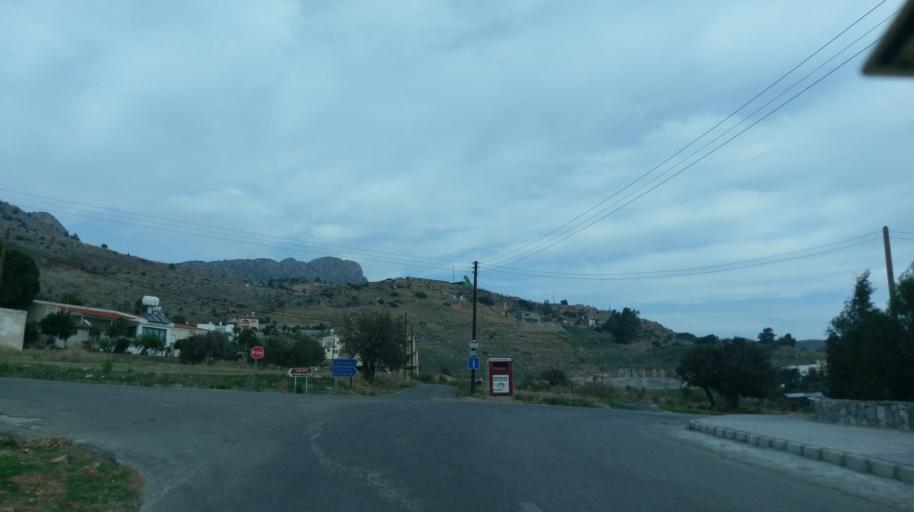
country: CY
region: Keryneia
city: Kyrenia
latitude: 35.2769
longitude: 33.3754
